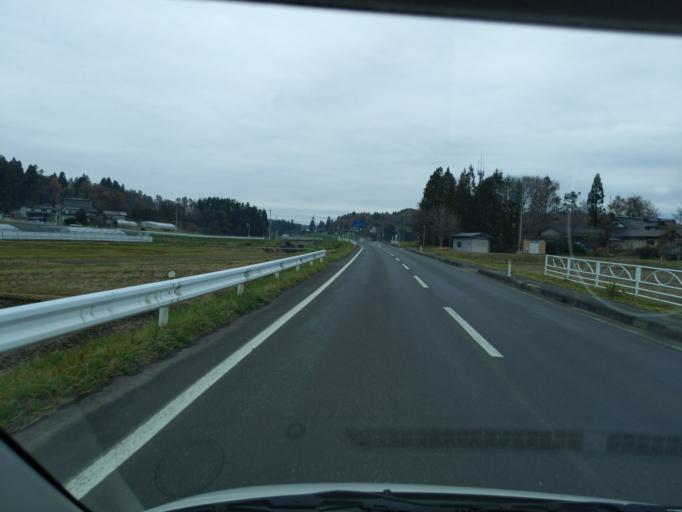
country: JP
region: Iwate
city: Mizusawa
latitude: 39.1890
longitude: 141.2225
